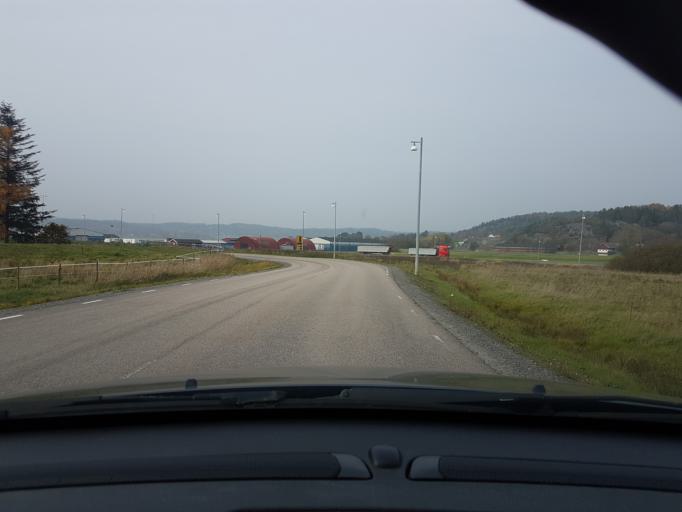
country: SE
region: Vaestra Goetaland
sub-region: Ale Kommun
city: Alvangen
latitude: 57.9669
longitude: 12.1492
